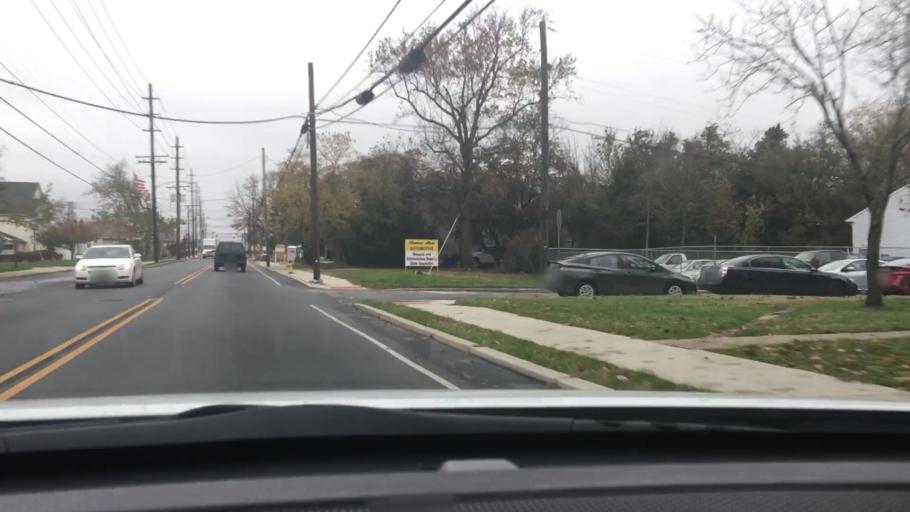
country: US
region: New Jersey
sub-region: Atlantic County
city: Pleasantville
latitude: 39.4065
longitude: -74.5170
